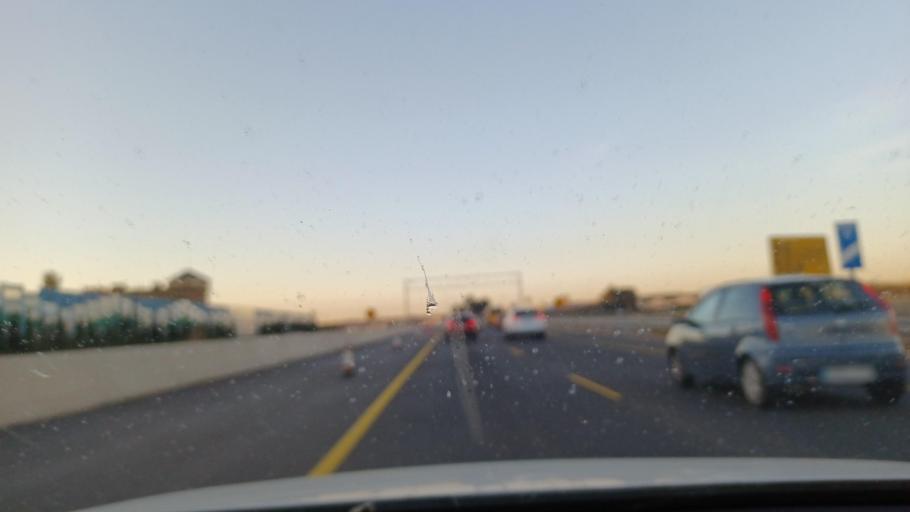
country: ES
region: Valencia
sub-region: Provincia de Valencia
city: Meliana
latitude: 39.5123
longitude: -0.3271
